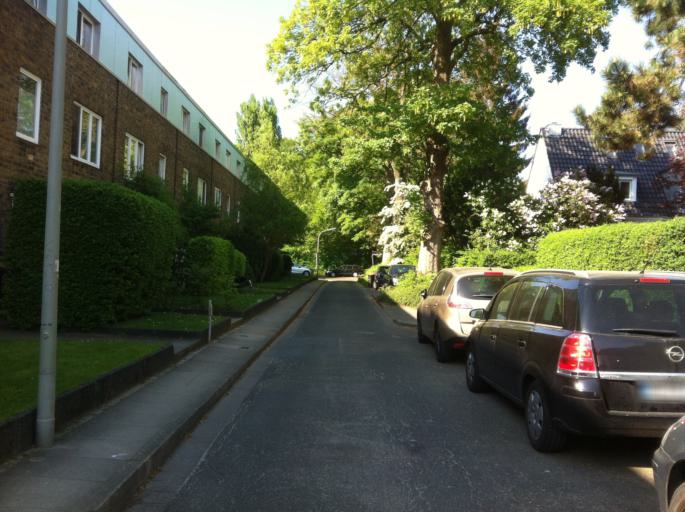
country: DE
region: Hamburg
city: Altona
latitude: 53.5478
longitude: 9.9122
